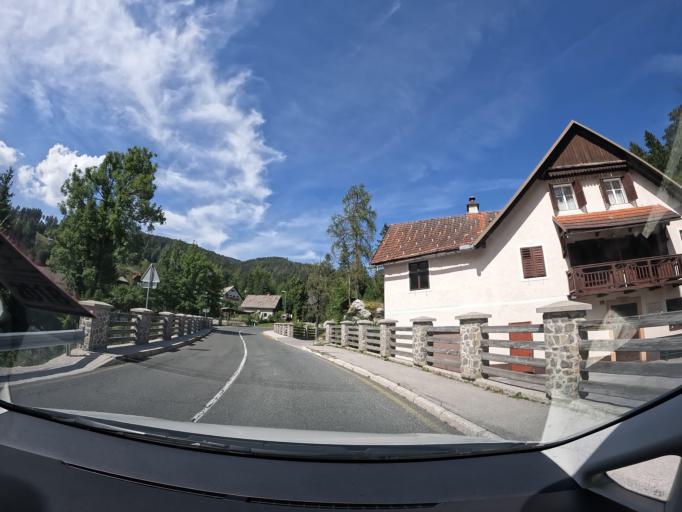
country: AT
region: Carinthia
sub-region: Politischer Bezirk Klagenfurt Land
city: Moosburg
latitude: 46.6586
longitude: 14.1357
